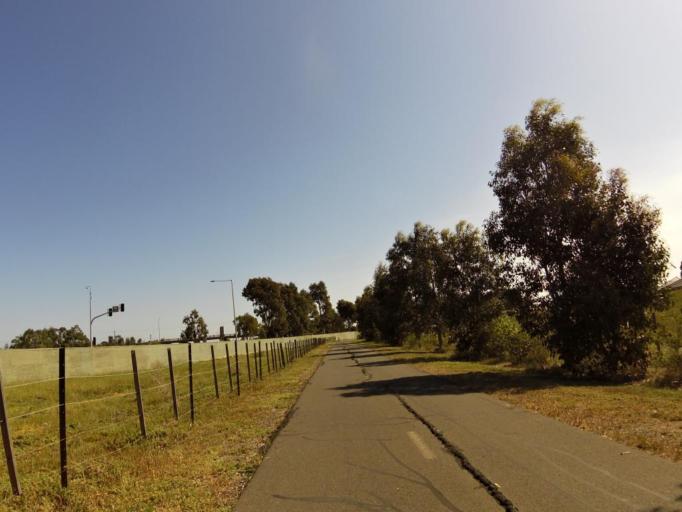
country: AU
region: Victoria
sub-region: Wyndham
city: Werribee
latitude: -37.9105
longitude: 144.6838
